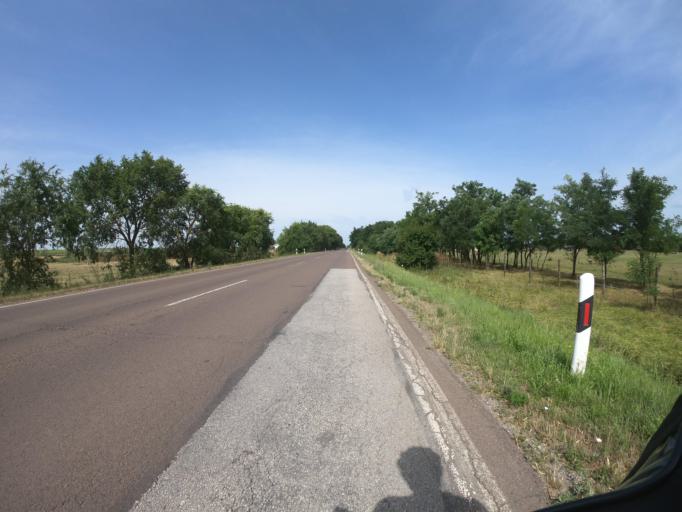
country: HU
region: Jasz-Nagykun-Szolnok
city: Tiszafured
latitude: 47.6016
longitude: 20.7965
